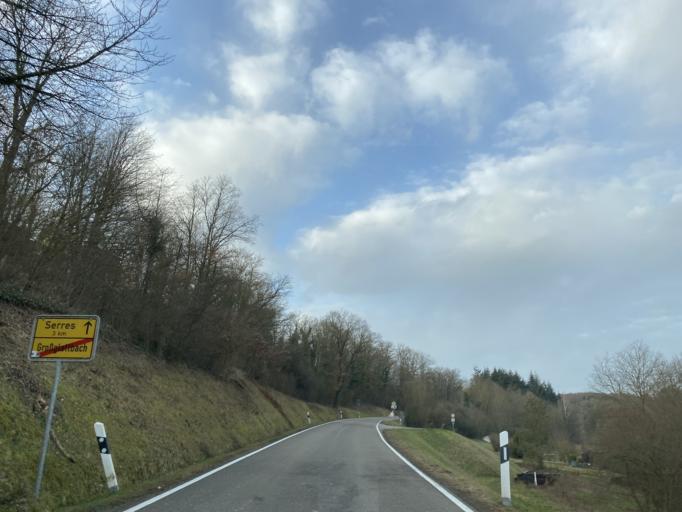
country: DE
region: Baden-Wuerttemberg
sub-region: Karlsruhe Region
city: Wiernsheim
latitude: 48.9111
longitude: 8.8936
